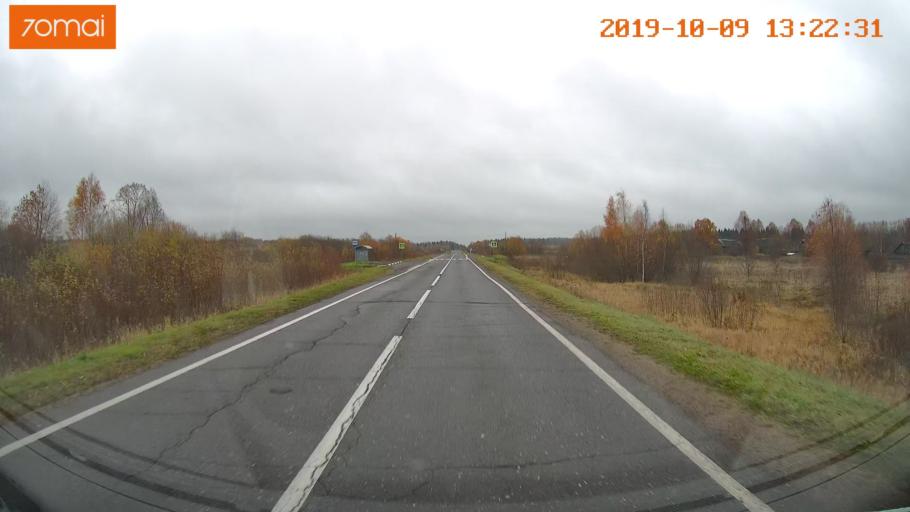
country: RU
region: Jaroslavl
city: Lyubim
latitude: 58.3399
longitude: 40.8651
